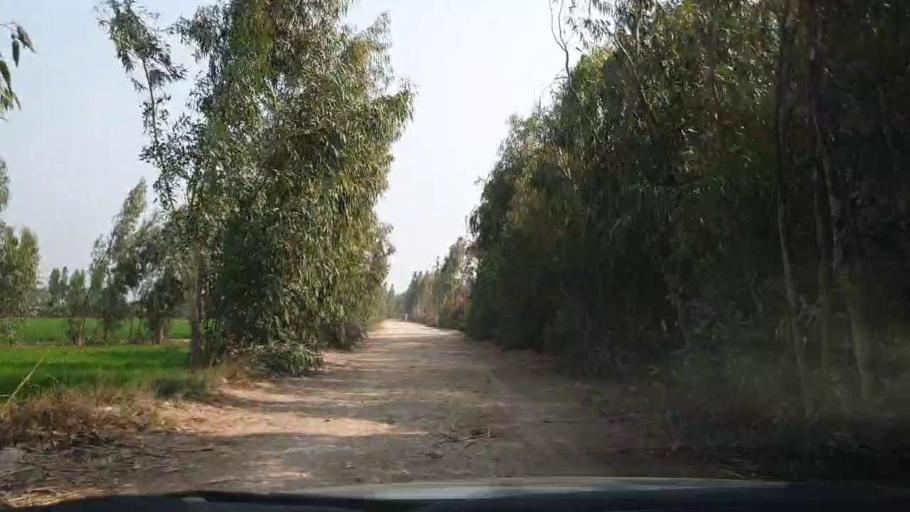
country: PK
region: Sindh
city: Matiari
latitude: 25.6474
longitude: 68.5542
